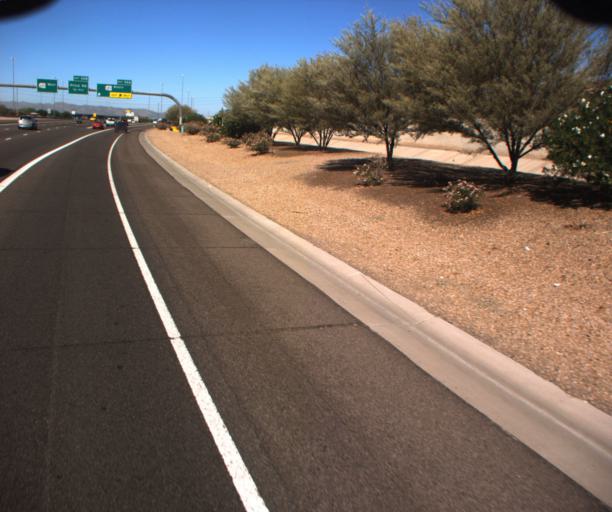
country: US
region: Arizona
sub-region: Maricopa County
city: Chandler
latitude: 33.2884
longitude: -111.8813
